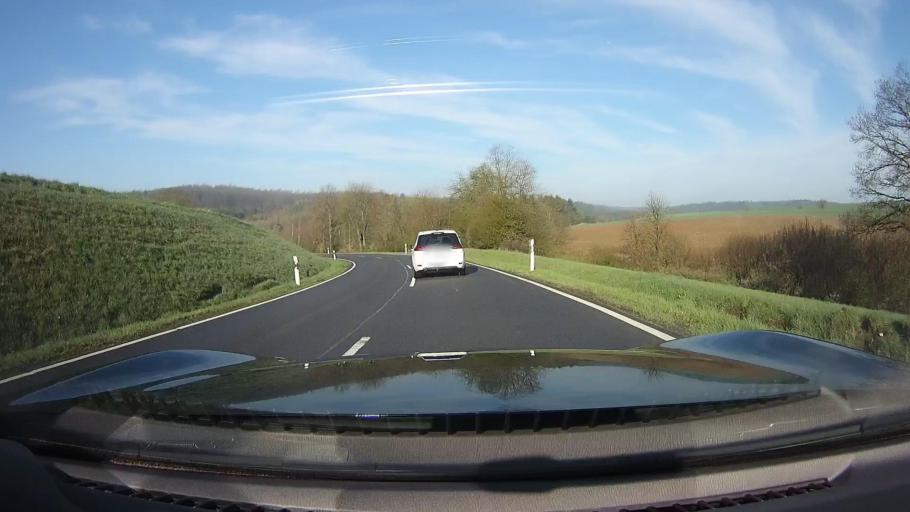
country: DE
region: Baden-Wuerttemberg
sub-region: Karlsruhe Region
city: Adelsheim
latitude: 49.4054
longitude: 9.3533
